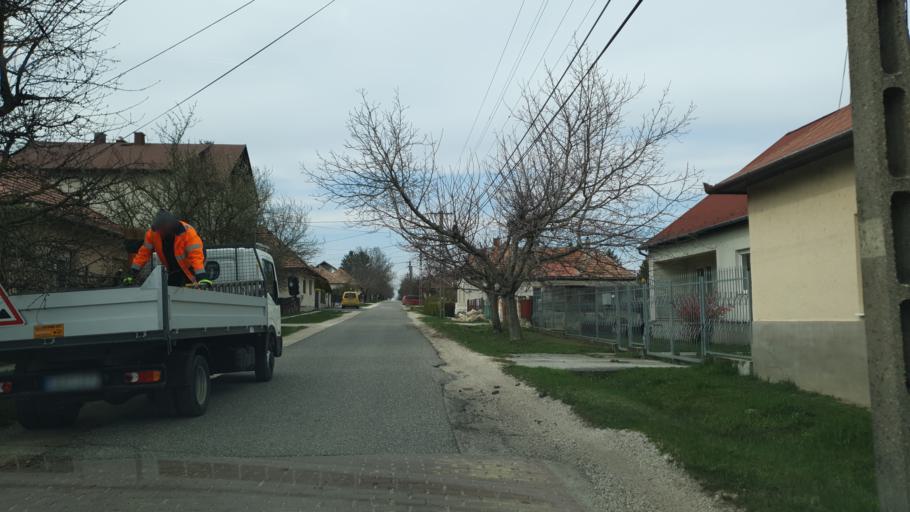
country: HU
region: Fejer
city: Etyek
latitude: 47.4509
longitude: 18.7585
